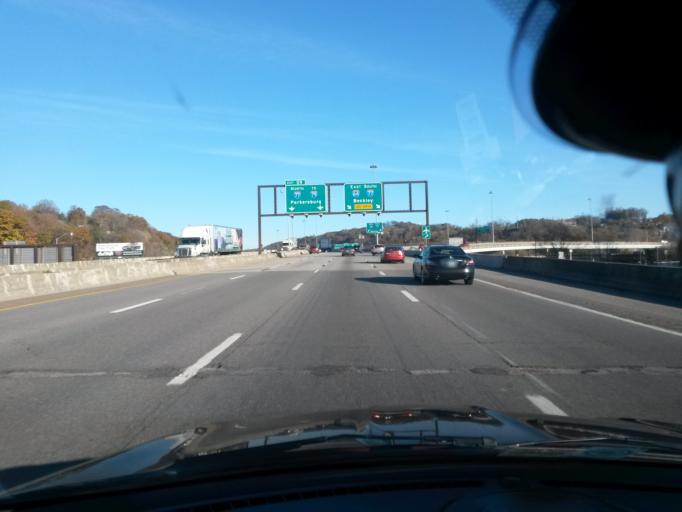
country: US
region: West Virginia
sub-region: Kanawha County
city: Charleston
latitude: 38.3601
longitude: -81.6360
